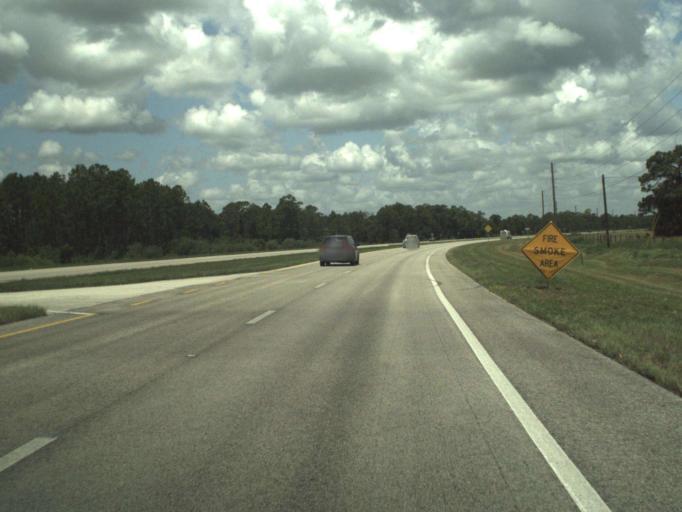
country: US
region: Florida
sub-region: Indian River County
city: Fellsmere
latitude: 27.6817
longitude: -80.8667
